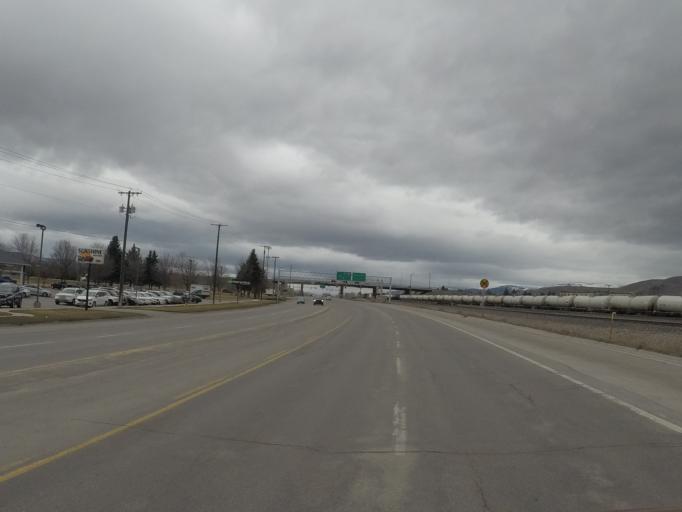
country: US
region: Montana
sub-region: Missoula County
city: Orchard Homes
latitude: 46.8968
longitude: -114.0349
